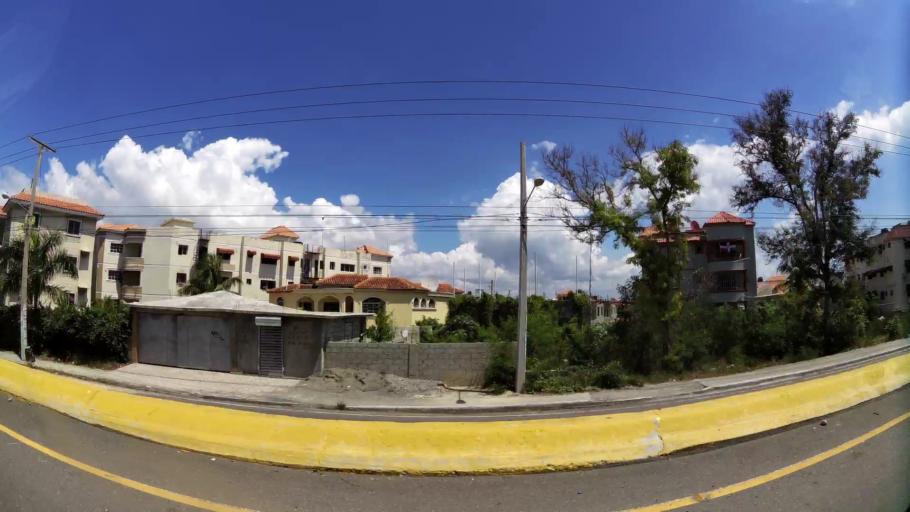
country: DO
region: Santo Domingo
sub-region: Santo Domingo
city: Santo Domingo Este
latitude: 18.4705
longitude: -69.8291
